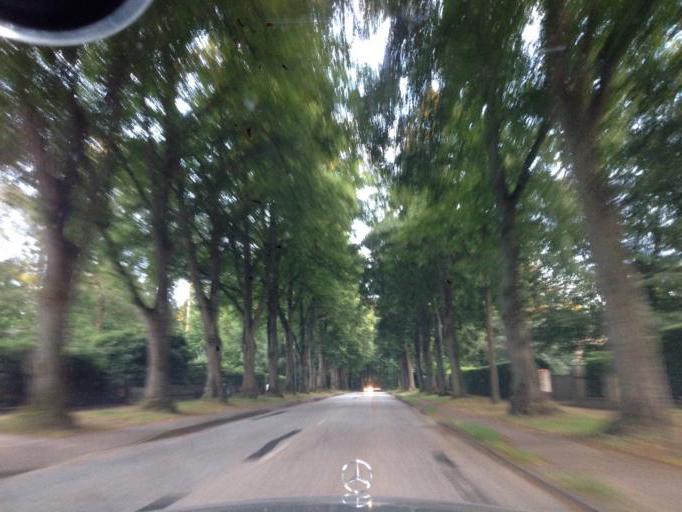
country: DE
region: Hamburg
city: Wohldorf-Ohlstedt
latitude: 53.6889
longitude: 10.1303
